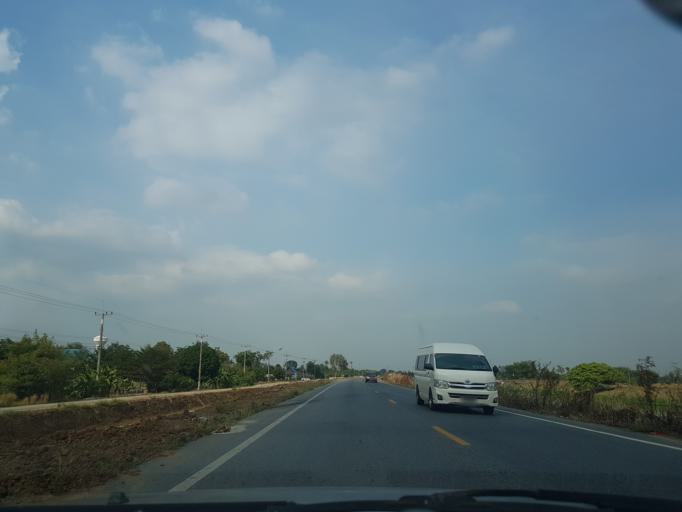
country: TH
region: Sara Buri
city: Nong Saeng
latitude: 14.5116
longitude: 100.7355
